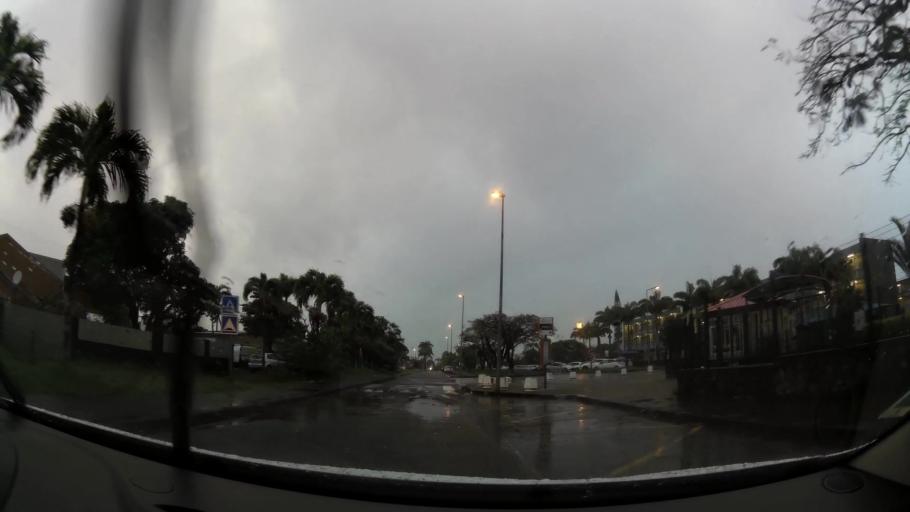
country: RE
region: Reunion
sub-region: Reunion
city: Saint-Benoit
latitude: -21.0419
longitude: 55.7187
